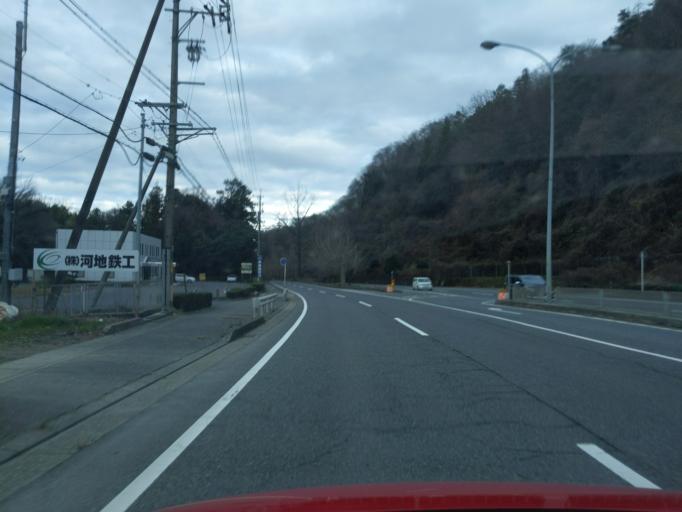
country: JP
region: Gifu
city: Tajimi
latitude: 35.3288
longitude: 137.0875
